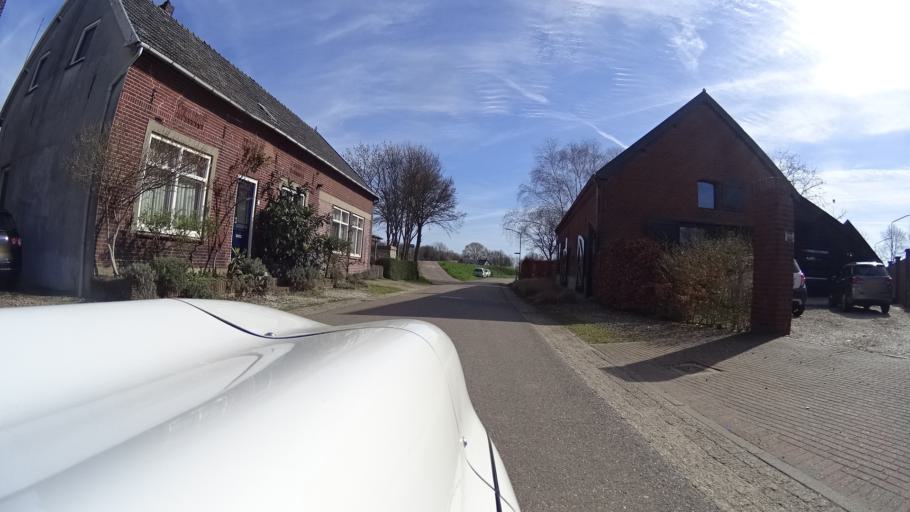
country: NL
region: North Brabant
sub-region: Gemeente Cuijk
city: Cuijk
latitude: 51.7141
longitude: 5.9110
